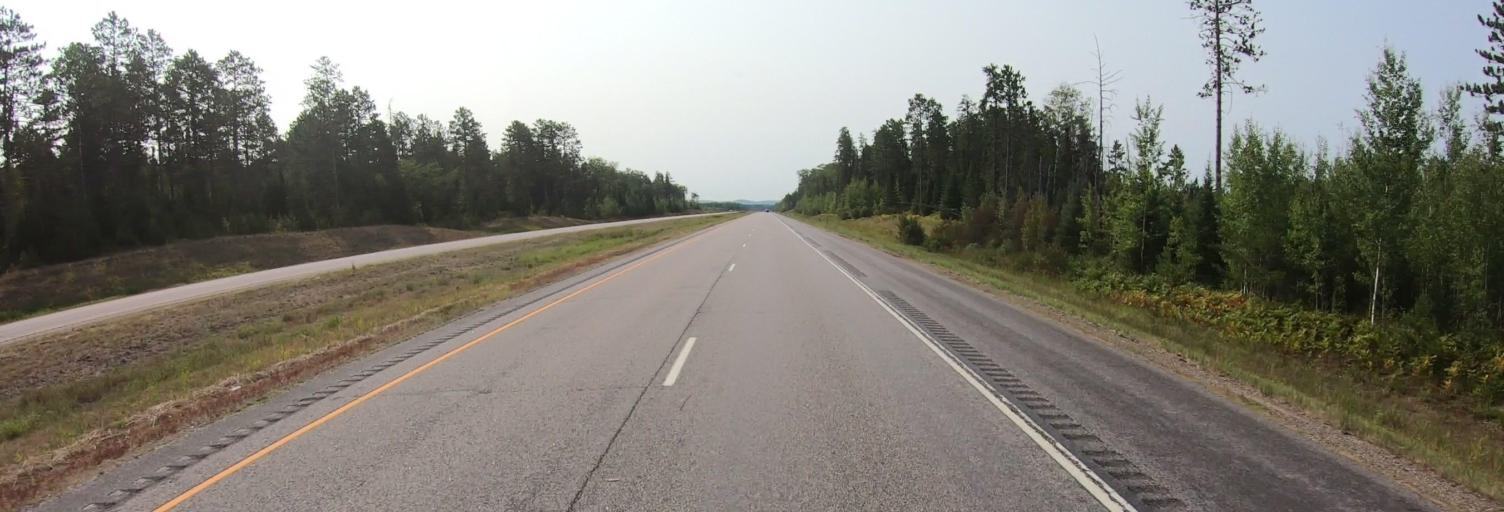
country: US
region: Minnesota
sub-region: Saint Louis County
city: Parkville
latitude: 47.6538
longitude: -92.5715
